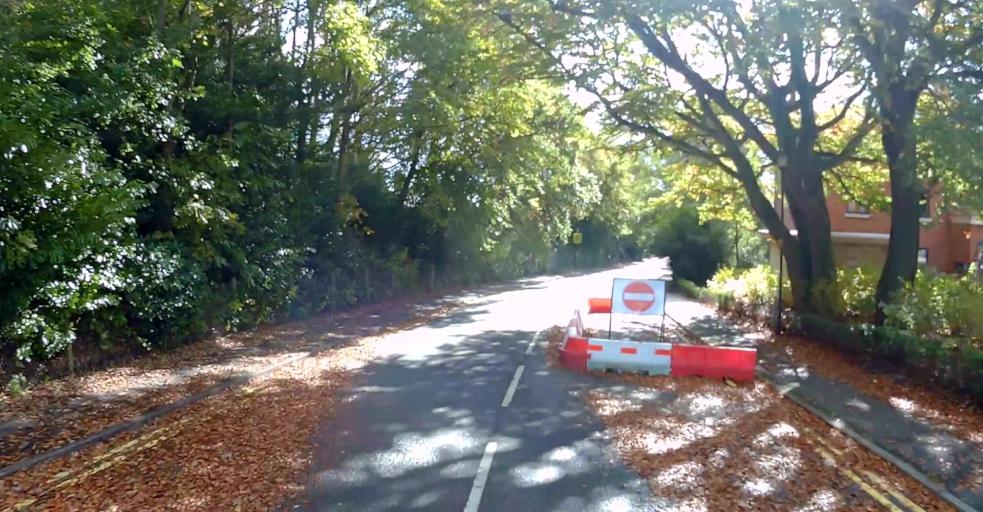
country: GB
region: England
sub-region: Hampshire
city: Aldershot
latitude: 51.2534
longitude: -0.7609
